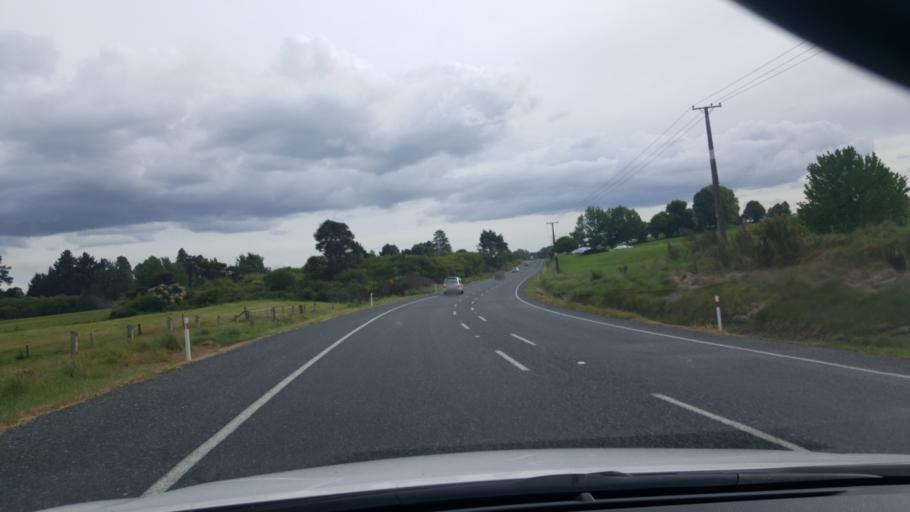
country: NZ
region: Waikato
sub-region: Taupo District
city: Taupo
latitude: -38.4748
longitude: 176.3048
